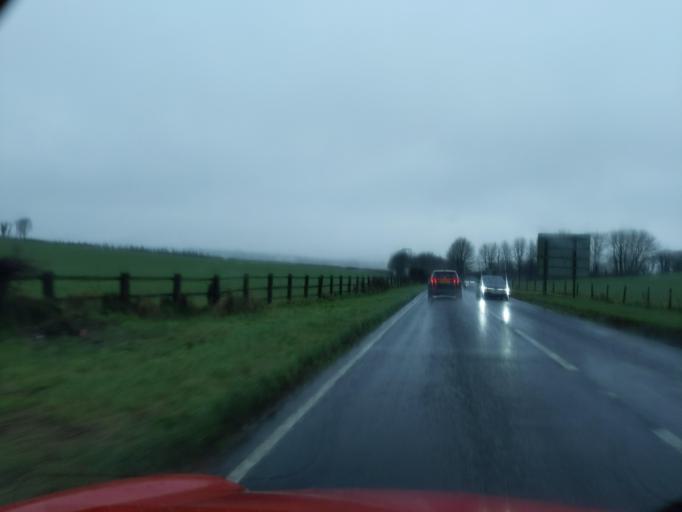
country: GB
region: England
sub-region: Cornwall
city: South Hill
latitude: 50.5499
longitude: -4.3326
